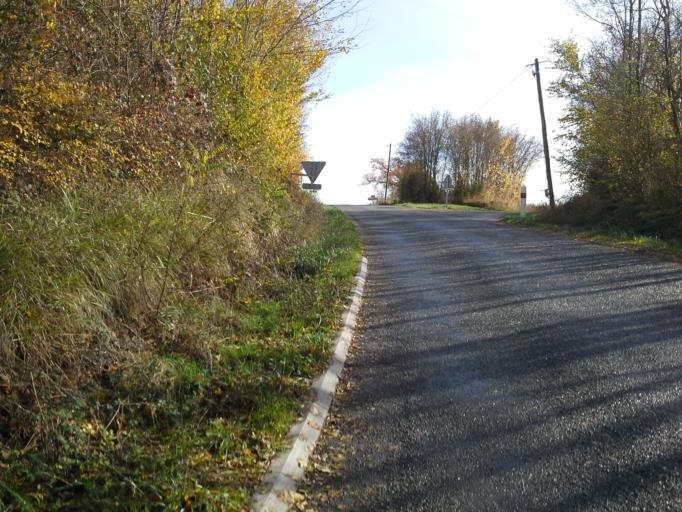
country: FR
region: Poitou-Charentes
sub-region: Departement de la Vienne
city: Pleumartin
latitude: 46.6427
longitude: 0.7583
